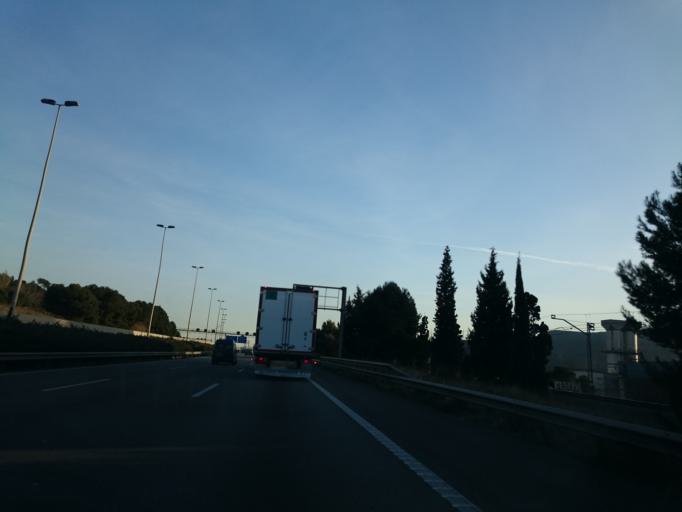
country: ES
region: Catalonia
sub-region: Provincia de Barcelona
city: Sant Andreu de la Barca
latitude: 41.4548
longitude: 1.9828
